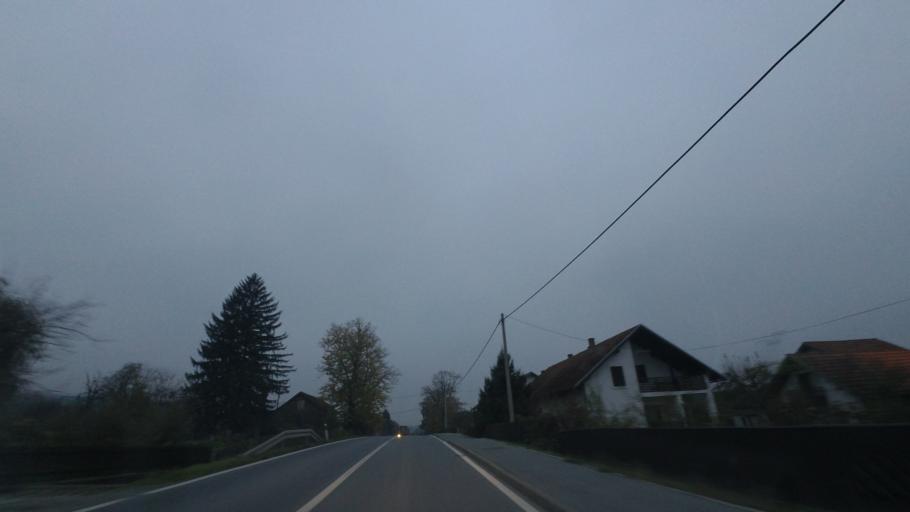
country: HR
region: Sisacko-Moslavacka
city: Petrinja
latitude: 45.4396
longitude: 16.2545
